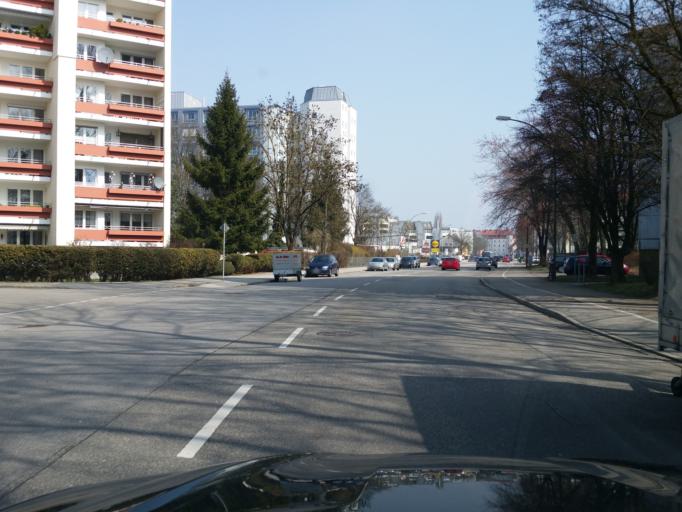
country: DE
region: Bavaria
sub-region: Lower Bavaria
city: Landshut
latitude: 48.5426
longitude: 12.1335
